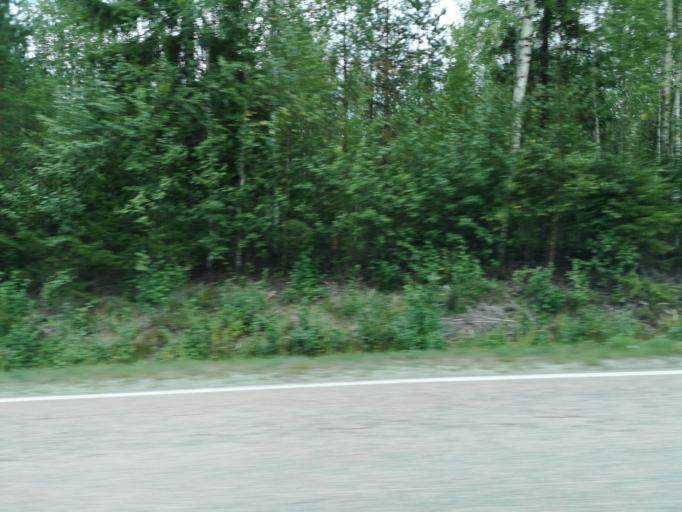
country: FI
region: Central Finland
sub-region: Jyvaeskylae
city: Hankasalmi
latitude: 62.3598
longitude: 26.5502
